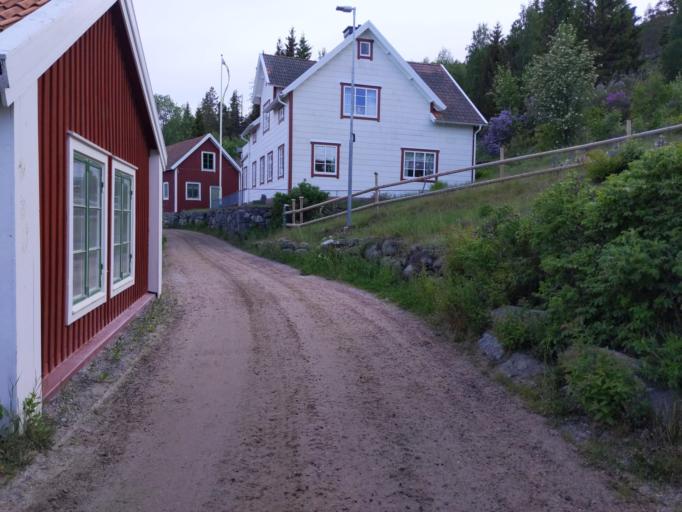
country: SE
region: Vaesternorrland
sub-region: OErnskoeldsviks Kommun
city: Kopmanholmen
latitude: 63.0212
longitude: 18.6472
